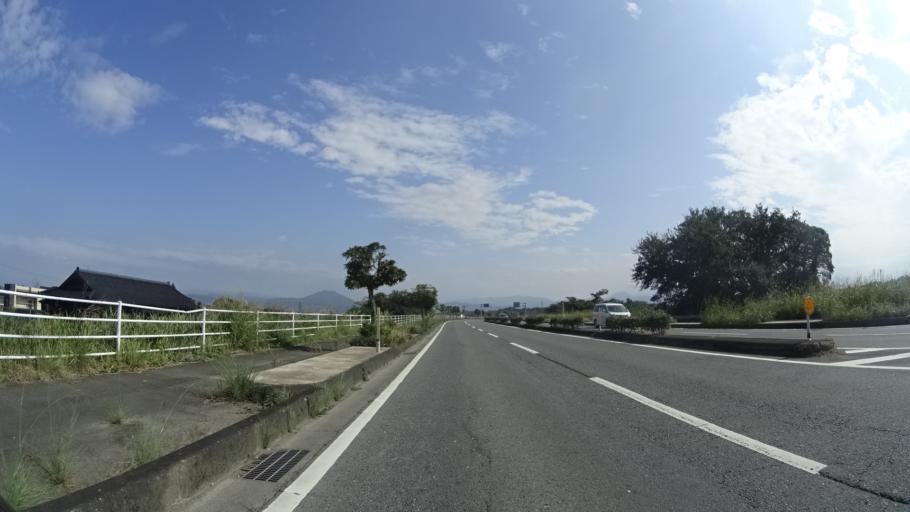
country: JP
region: Kumamoto
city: Kumamoto
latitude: 32.7352
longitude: 130.7516
